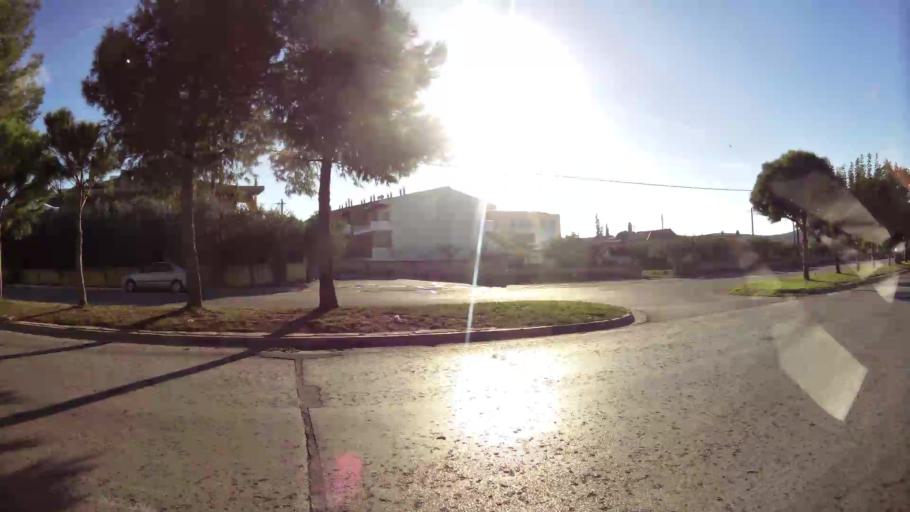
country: GR
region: Attica
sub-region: Nomarchia Anatolikis Attikis
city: Kalyvia Thorikou
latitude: 37.8452
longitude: 23.9255
